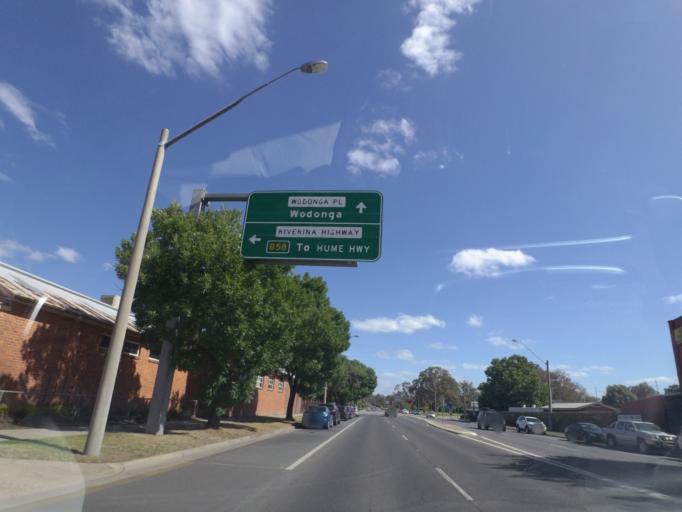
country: AU
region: New South Wales
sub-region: Albury Municipality
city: South Albury
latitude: -36.0831
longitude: 146.9101
